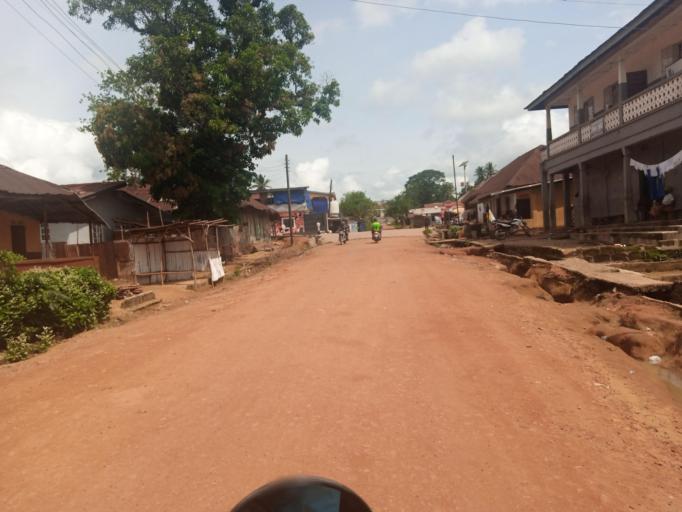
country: SL
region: Southern Province
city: Bo
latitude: 7.9690
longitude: -11.7384
